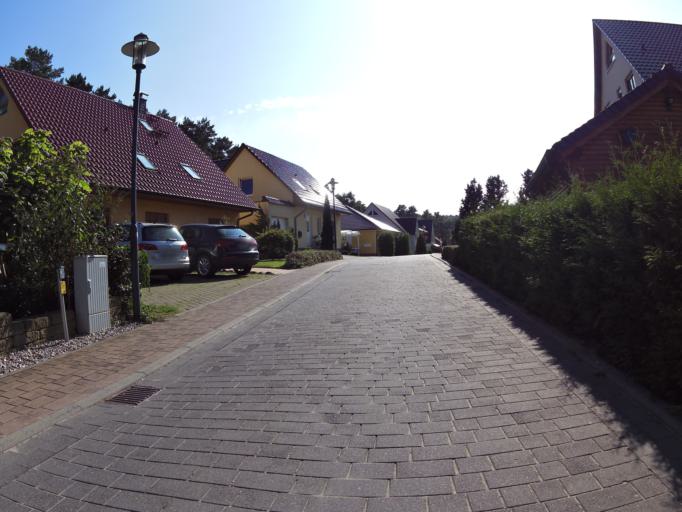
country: DE
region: Mecklenburg-Vorpommern
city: Seebad Heringsdorf
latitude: 53.9340
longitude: 14.1977
